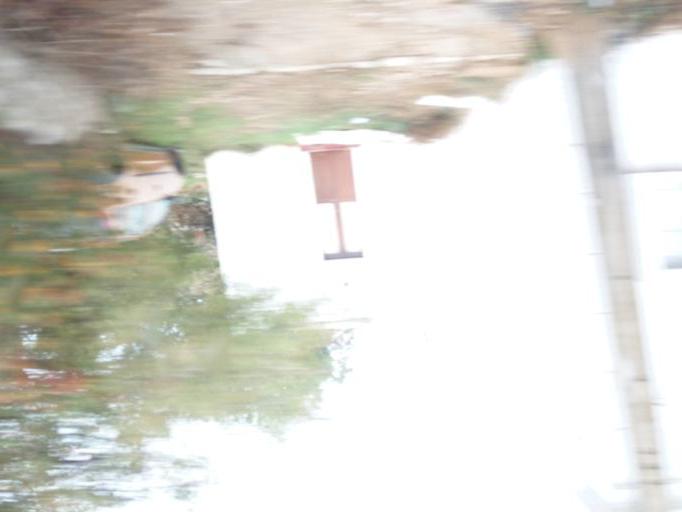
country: PT
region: Faro
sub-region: Faro
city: Santa Barbara de Nexe
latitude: 37.1046
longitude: -7.9978
